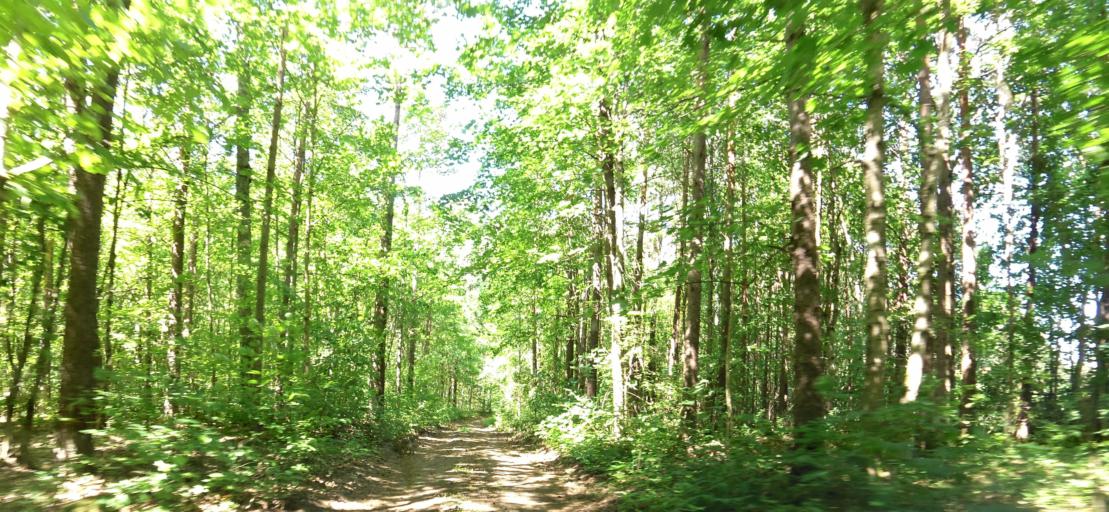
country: LT
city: Grigiskes
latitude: 54.7887
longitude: 24.9663
